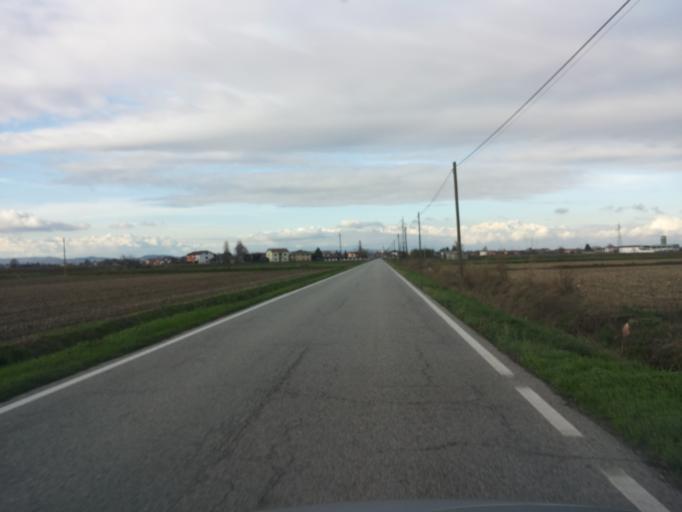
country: IT
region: Piedmont
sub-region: Provincia di Vercelli
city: Tronzano Vercellese
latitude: 45.3316
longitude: 8.1862
